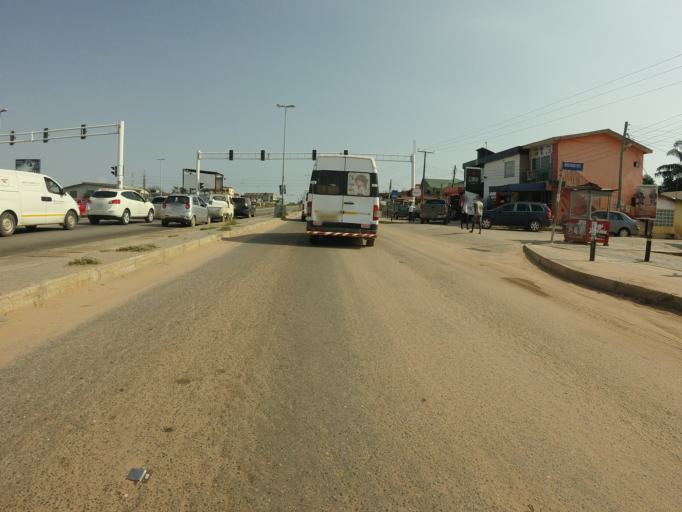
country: GH
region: Greater Accra
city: Gbawe
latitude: 5.6012
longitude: -0.2924
